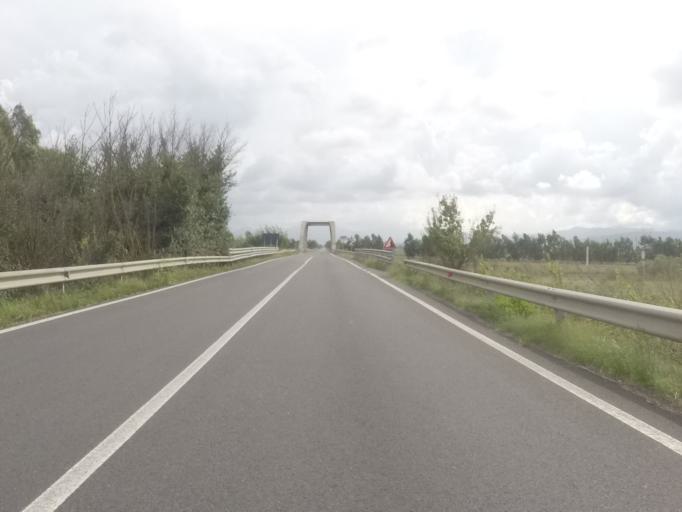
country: IT
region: Sardinia
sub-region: Provincia di Oristano
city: San Nicolo d'Arcidano
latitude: 39.6766
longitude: 8.6513
